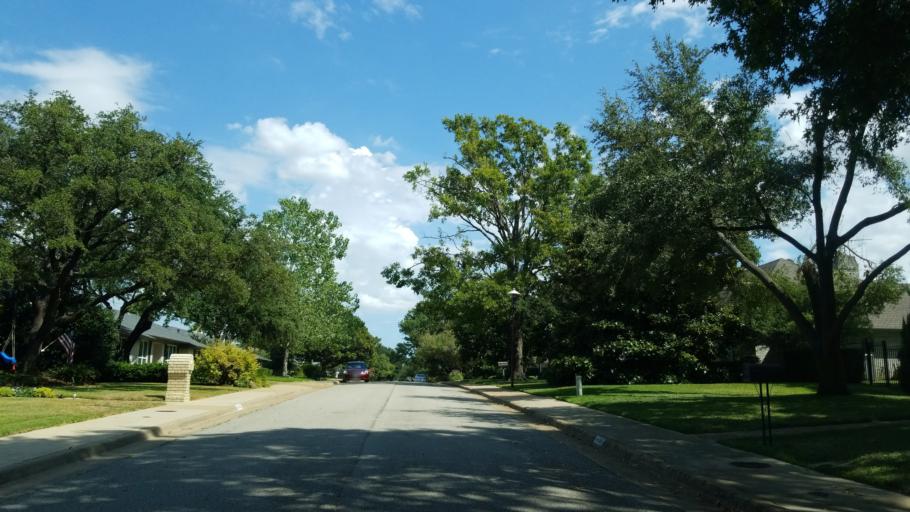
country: US
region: Texas
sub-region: Dallas County
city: Addison
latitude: 32.9515
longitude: -96.7907
